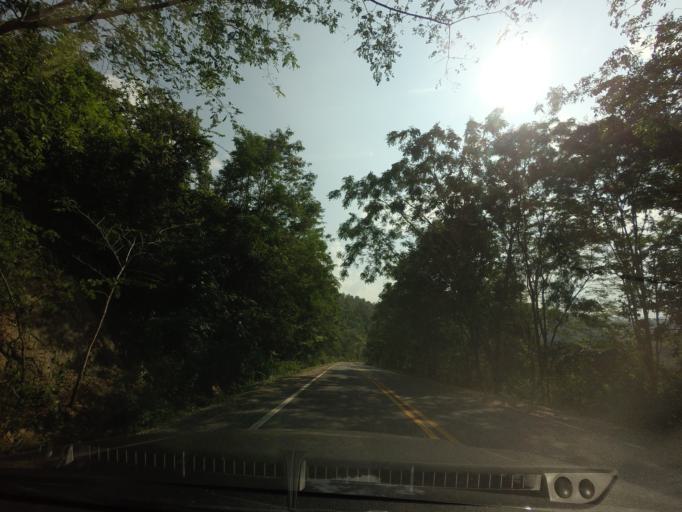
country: TH
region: Nan
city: Na Noi
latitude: 18.2787
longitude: 100.9674
